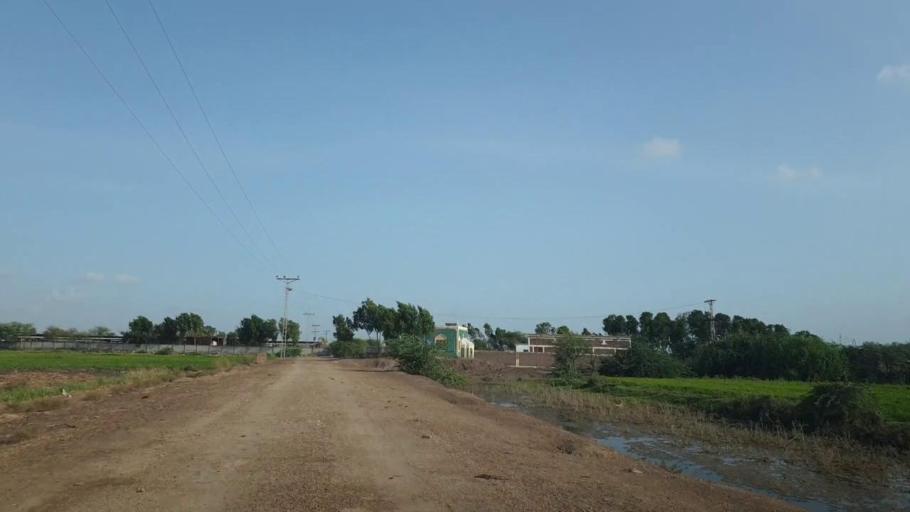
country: PK
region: Sindh
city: Kadhan
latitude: 24.6237
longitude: 69.0853
